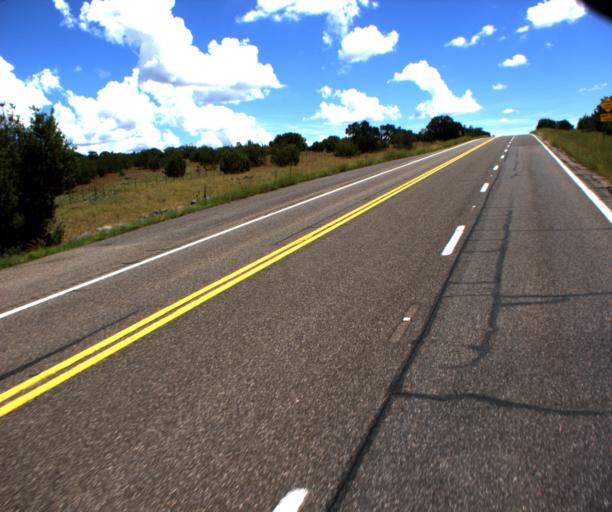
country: US
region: Arizona
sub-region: Gila County
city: Pine
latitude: 34.4910
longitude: -111.6267
